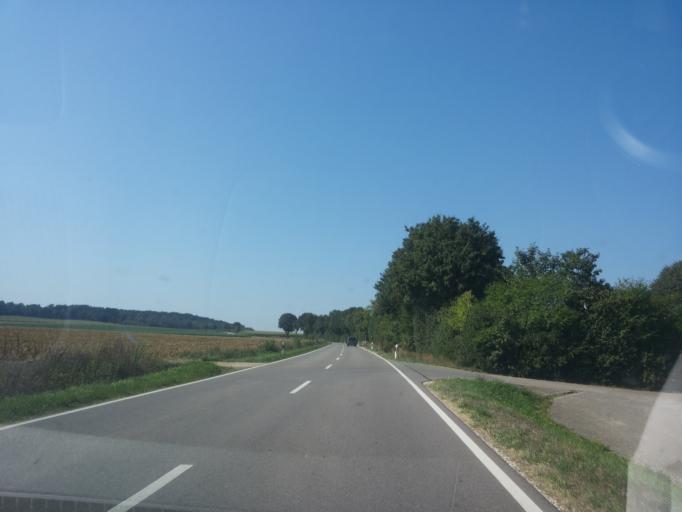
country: DE
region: Bavaria
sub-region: Lower Bavaria
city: Essing
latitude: 48.8838
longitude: 11.8037
